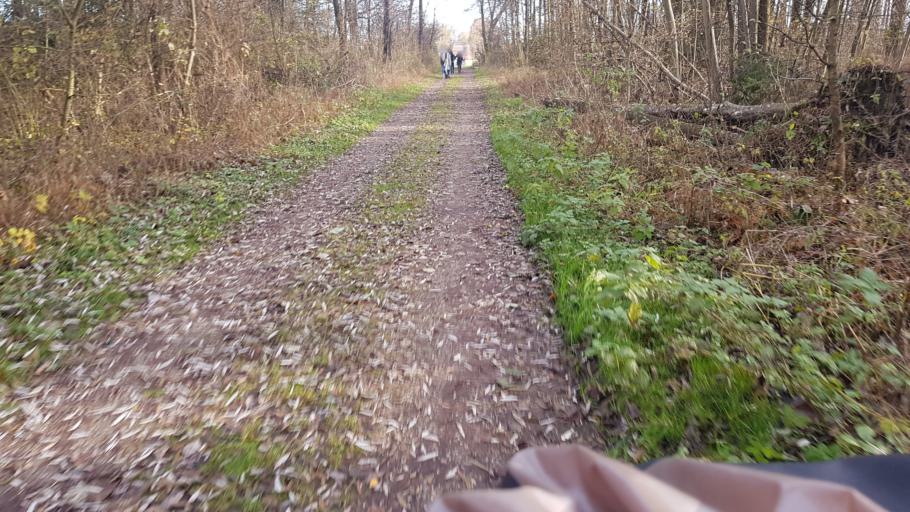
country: DE
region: Bavaria
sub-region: Upper Bavaria
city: Oberschleissheim
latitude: 48.2462
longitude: 11.5279
